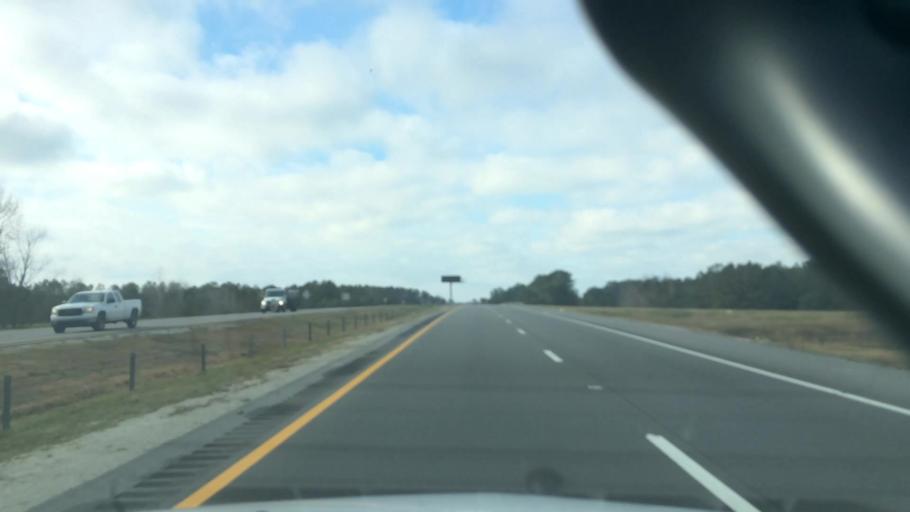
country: US
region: North Carolina
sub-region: New Hanover County
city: Wrightsboro
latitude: 34.3166
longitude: -77.9191
